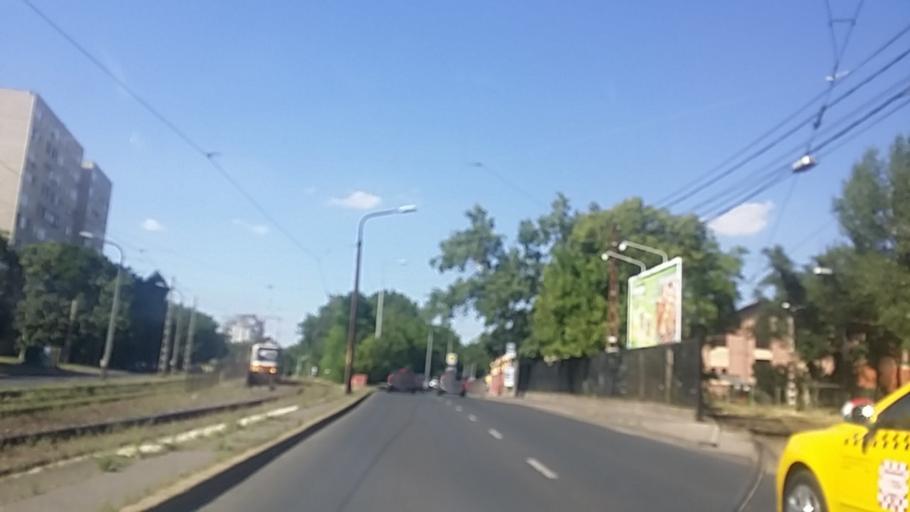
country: HU
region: Budapest
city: Budapest IV. keruelet
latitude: 47.5508
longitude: 19.0915
